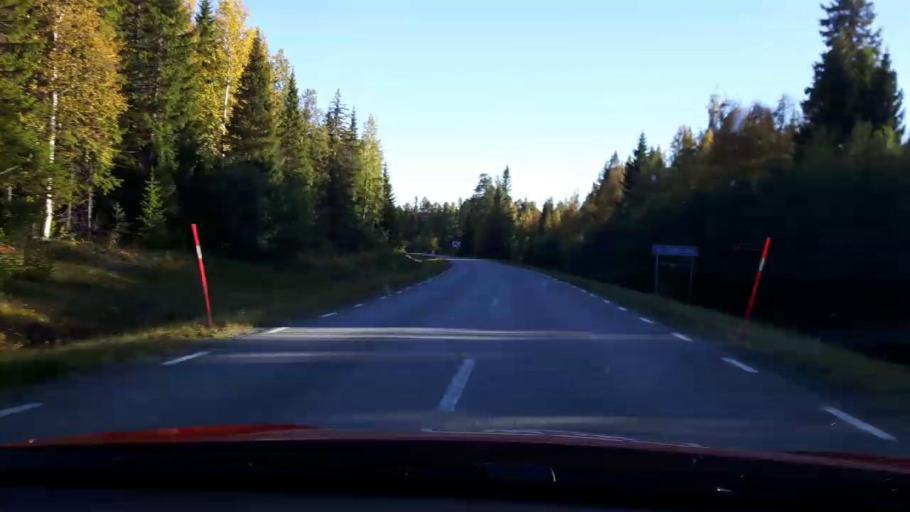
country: SE
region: Jaemtland
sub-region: OEstersunds Kommun
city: Lit
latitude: 63.7530
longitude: 14.7153
